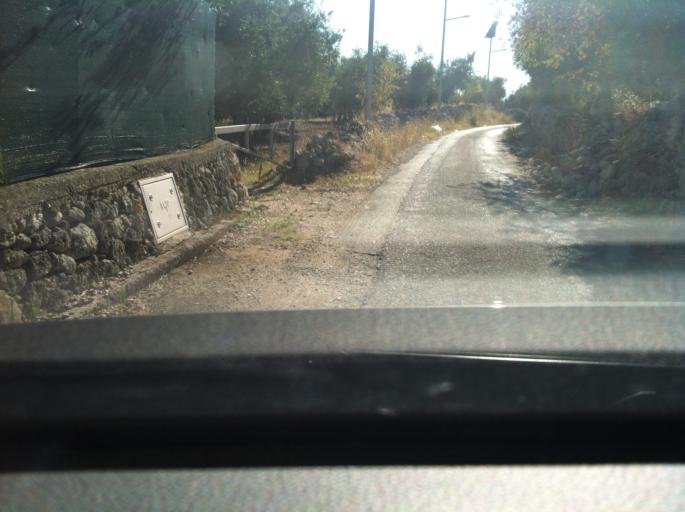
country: IT
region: Apulia
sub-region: Provincia di Foggia
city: Monte Sant'Angelo
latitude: 41.6547
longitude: 15.9656
